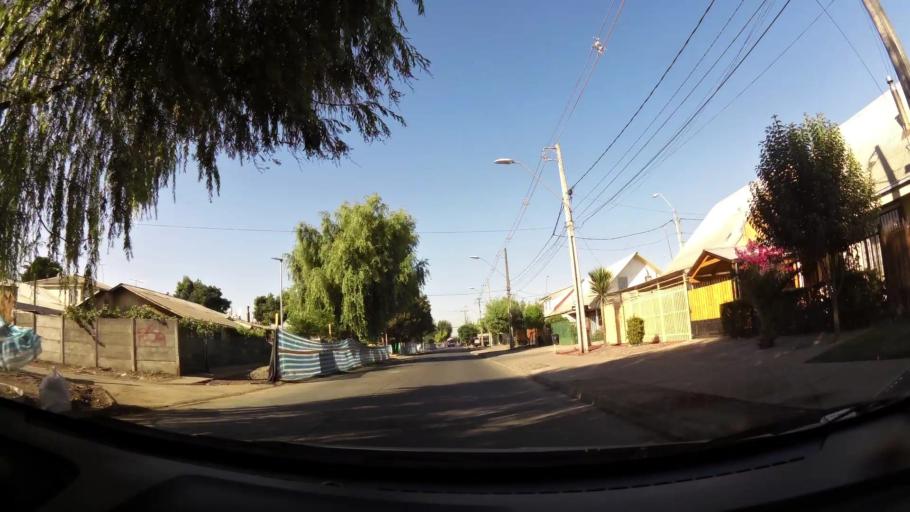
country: CL
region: Maule
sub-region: Provincia de Curico
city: Curico
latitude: -34.9938
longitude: -71.2557
